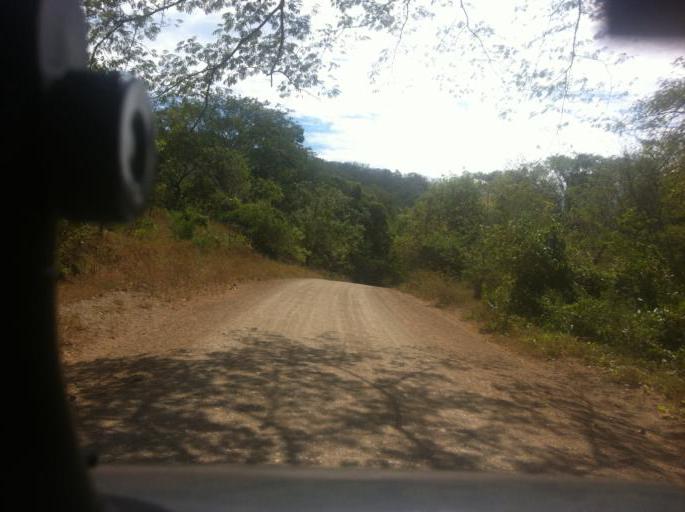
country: NI
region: Rivas
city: Belen
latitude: 11.5713
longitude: -86.0260
